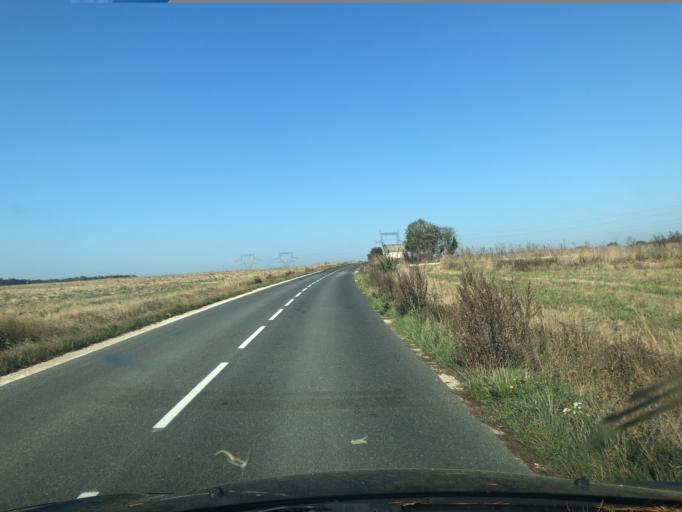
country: FR
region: Centre
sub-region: Departement d'Indre-et-Loire
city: Cerelles
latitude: 47.4896
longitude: 0.6598
